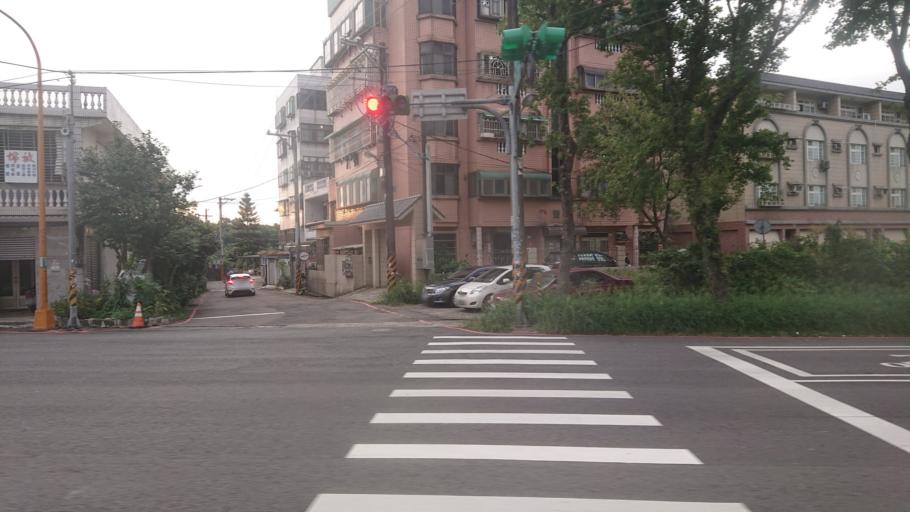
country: TW
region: Taiwan
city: Daxi
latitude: 24.8804
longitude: 121.2622
